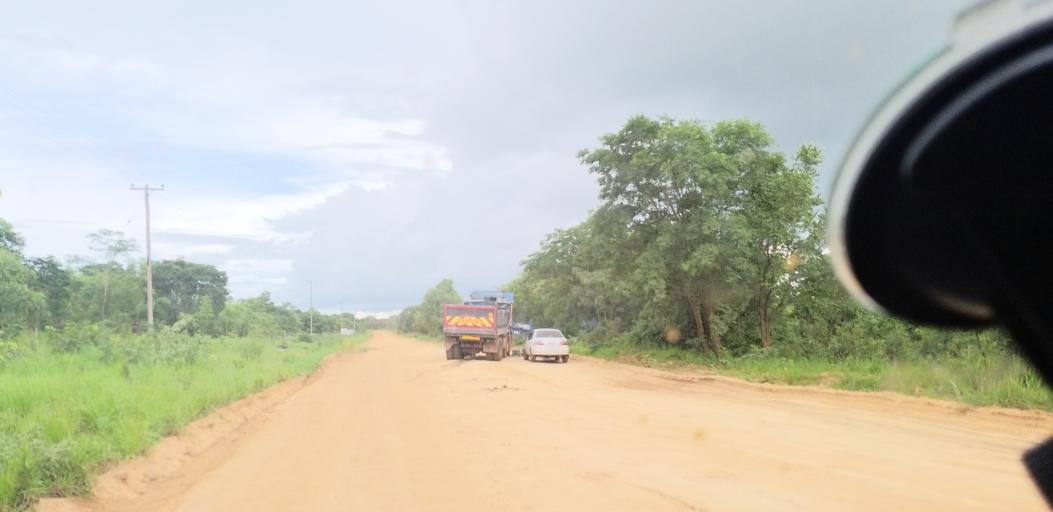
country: ZM
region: Lusaka
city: Chongwe
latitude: -15.1792
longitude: 28.4543
